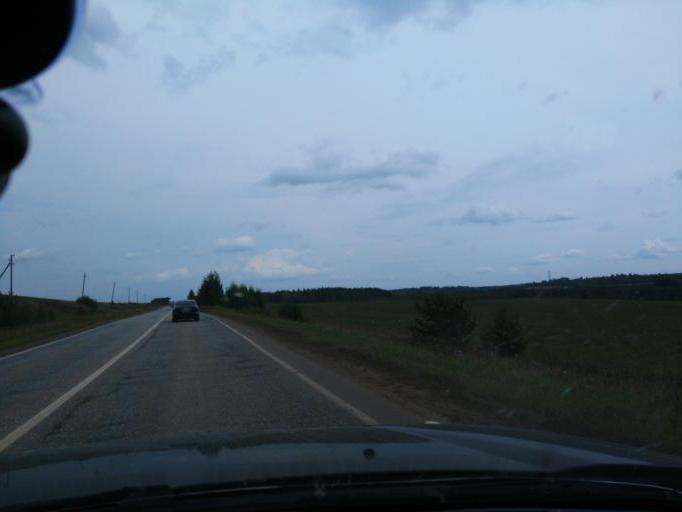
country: RU
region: Perm
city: Kuyeda
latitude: 56.4705
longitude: 55.7406
